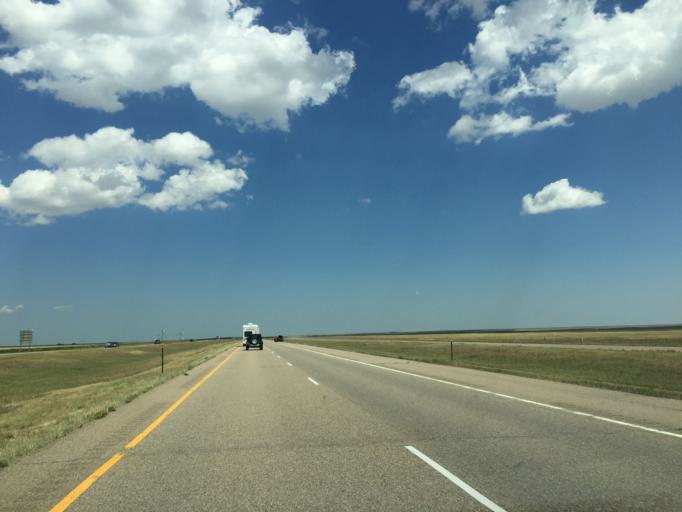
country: US
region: Colorado
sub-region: Lincoln County
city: Hugo
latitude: 39.2769
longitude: -103.4703
